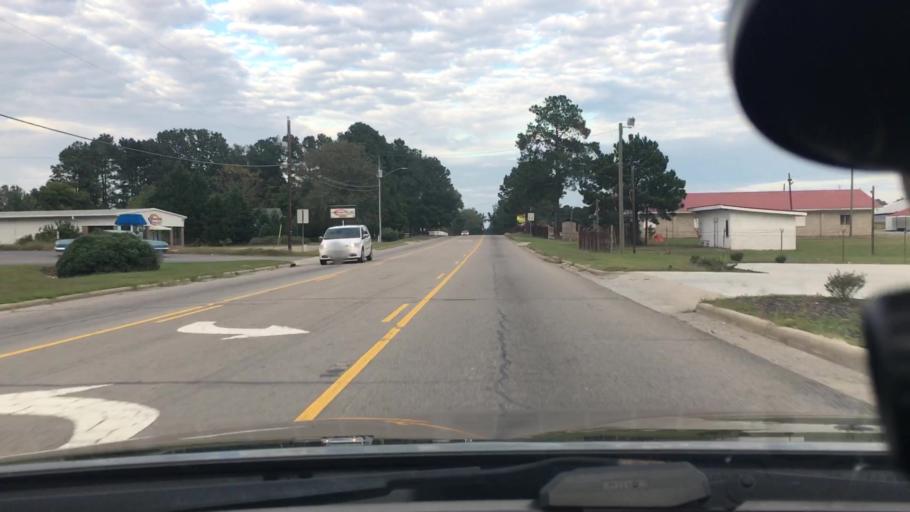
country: US
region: North Carolina
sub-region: Moore County
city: Carthage
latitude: 35.3442
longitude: -79.3916
